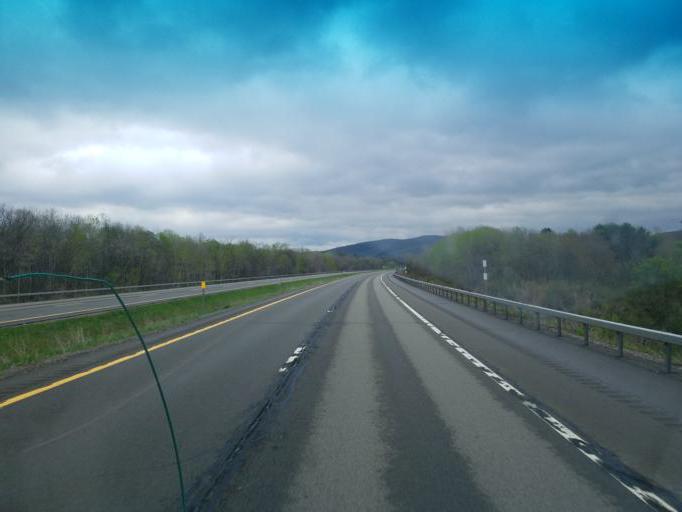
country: US
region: New York
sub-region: Cattaraugus County
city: Randolph
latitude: 42.1037
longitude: -78.8730
